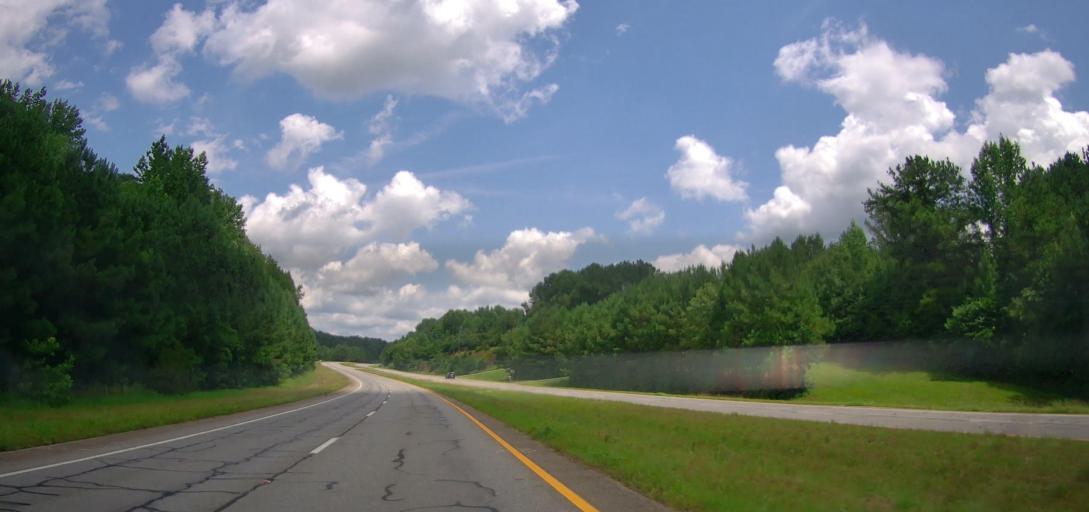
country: US
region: Georgia
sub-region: Heard County
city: Franklin
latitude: 33.2584
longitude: -85.0615
